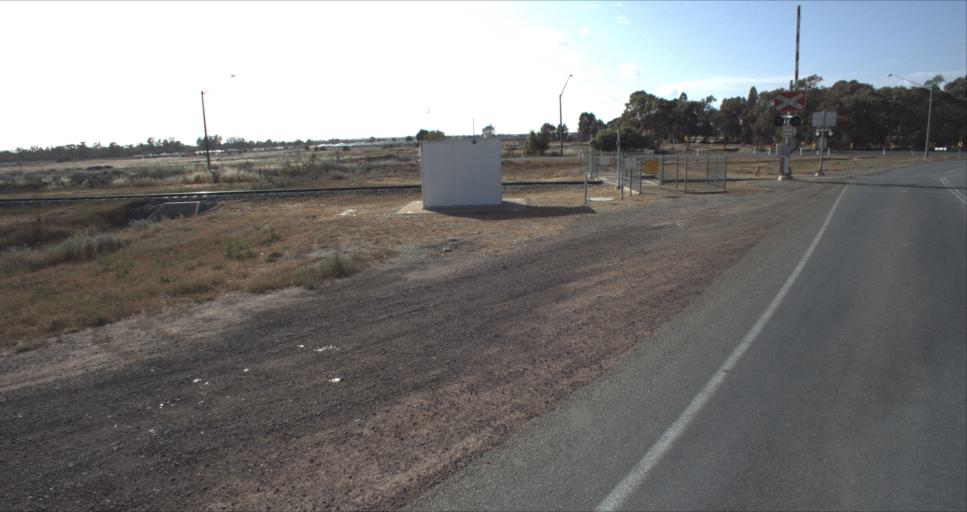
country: AU
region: New South Wales
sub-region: Leeton
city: Leeton
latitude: -34.5686
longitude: 146.3940
